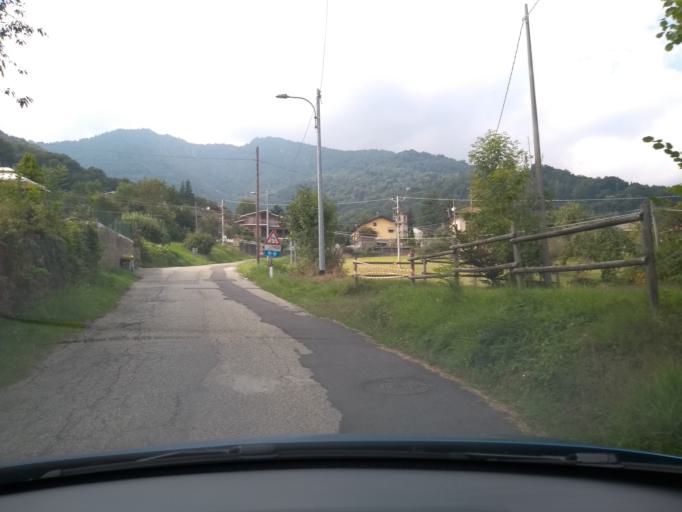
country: IT
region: Piedmont
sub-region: Provincia di Torino
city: Corio
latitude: 45.3167
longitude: 7.5222
